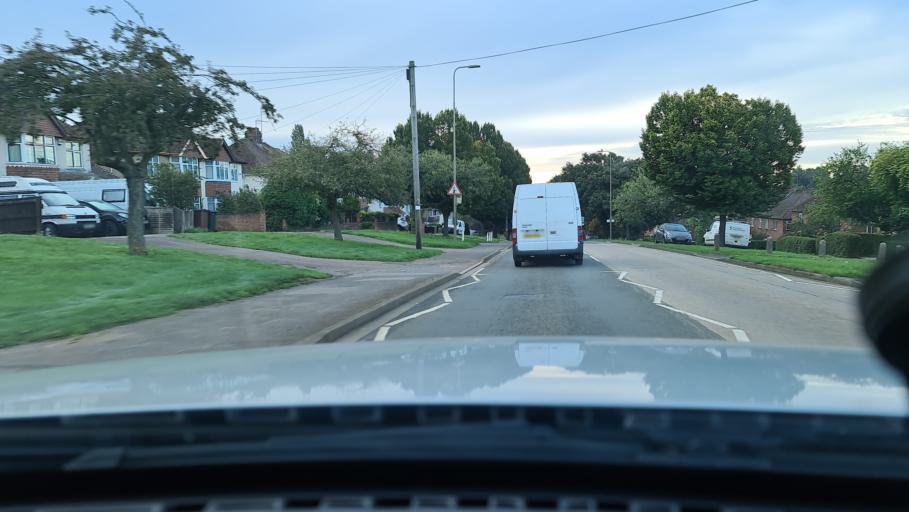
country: GB
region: England
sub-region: Oxfordshire
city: Banbury
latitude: 52.0680
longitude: -1.3590
